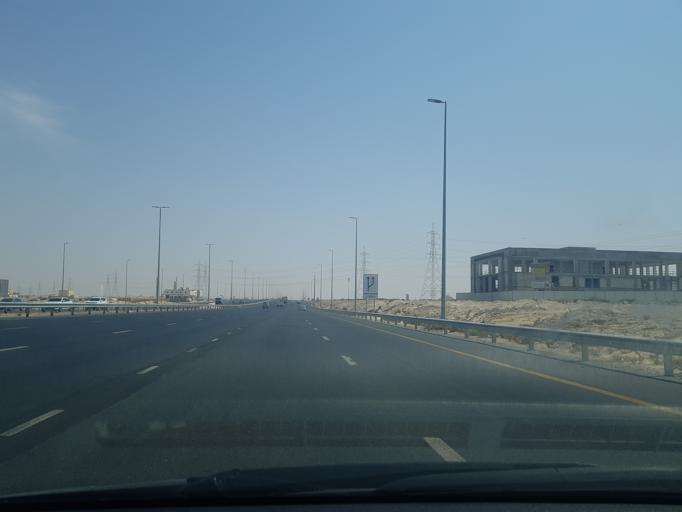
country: AE
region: Ash Shariqah
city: Sharjah
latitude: 25.2440
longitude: 55.5510
